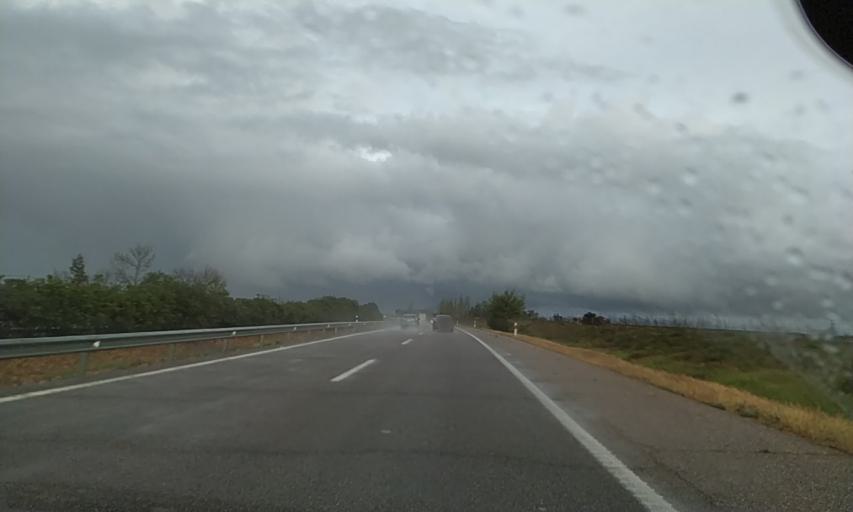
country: ES
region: Extremadura
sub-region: Provincia de Badajoz
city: Talavera La Real
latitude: 38.8565
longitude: -6.7429
